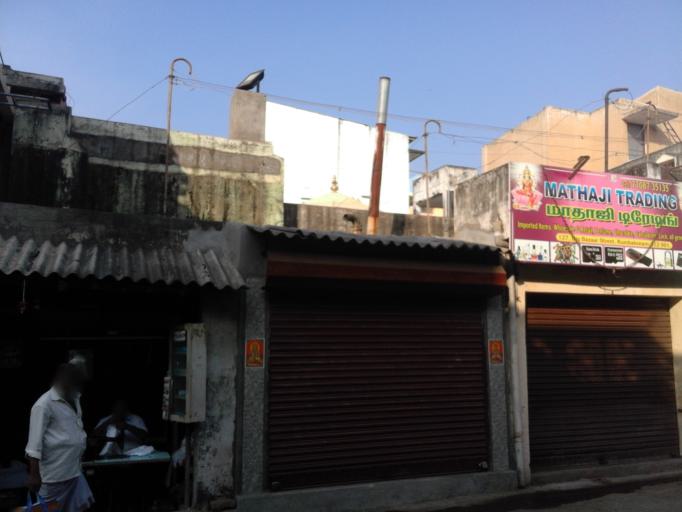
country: IN
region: Tamil Nadu
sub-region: Thanjavur
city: Kumbakonam
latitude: 10.9614
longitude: 79.3728
